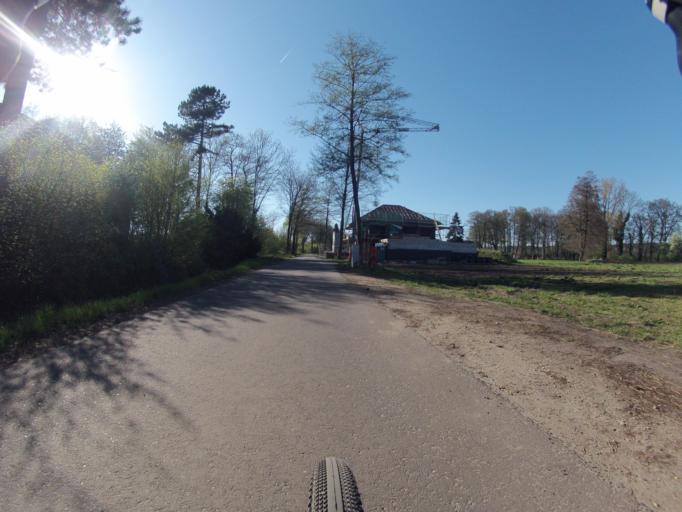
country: DE
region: North Rhine-Westphalia
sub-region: Regierungsbezirk Munster
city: Birgte
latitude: 52.2323
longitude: 7.6888
